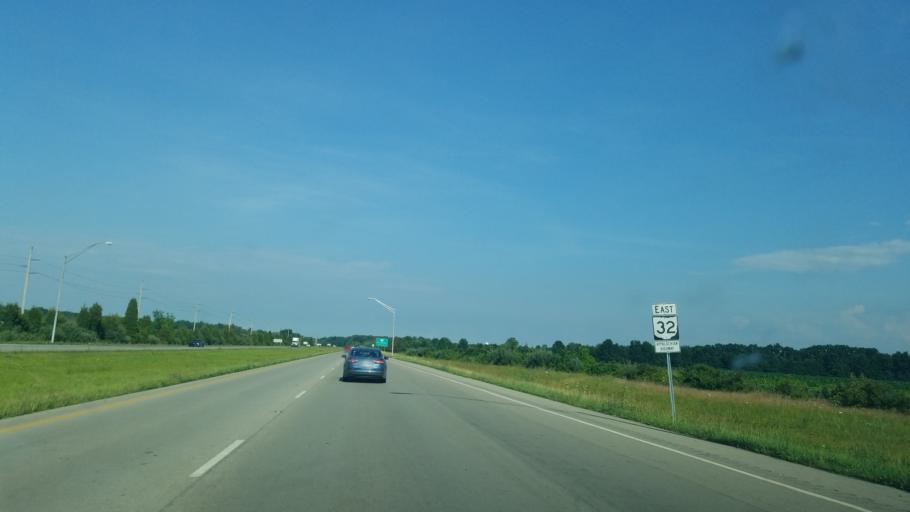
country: US
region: Ohio
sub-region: Clermont County
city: Williamsburg
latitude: 39.0691
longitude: -84.0886
